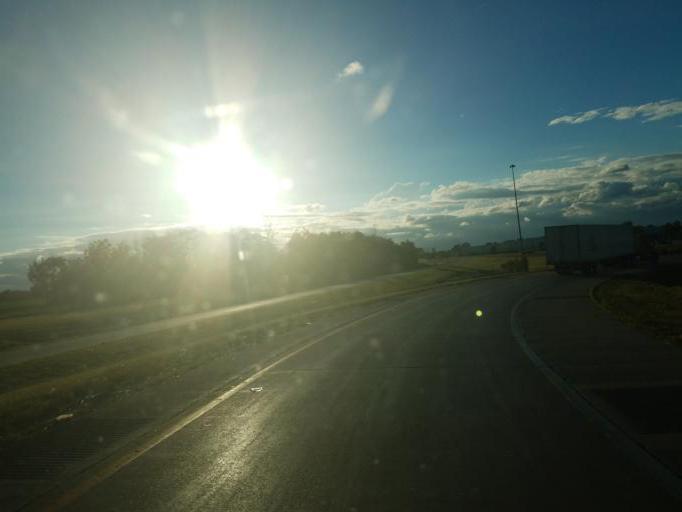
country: US
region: Indiana
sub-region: Allen County
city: New Haven
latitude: 41.0620
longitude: -84.9911
